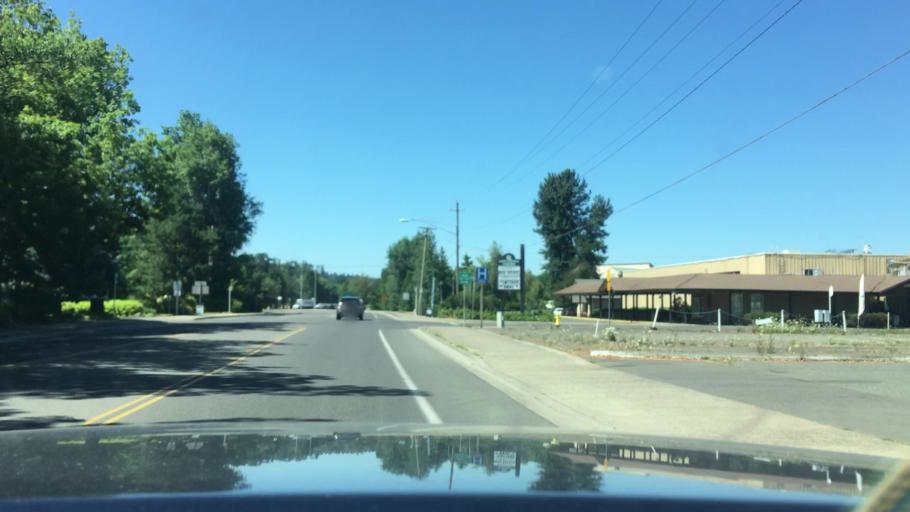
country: US
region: Oregon
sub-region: Lane County
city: Cottage Grove
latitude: 43.8016
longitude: -123.0401
